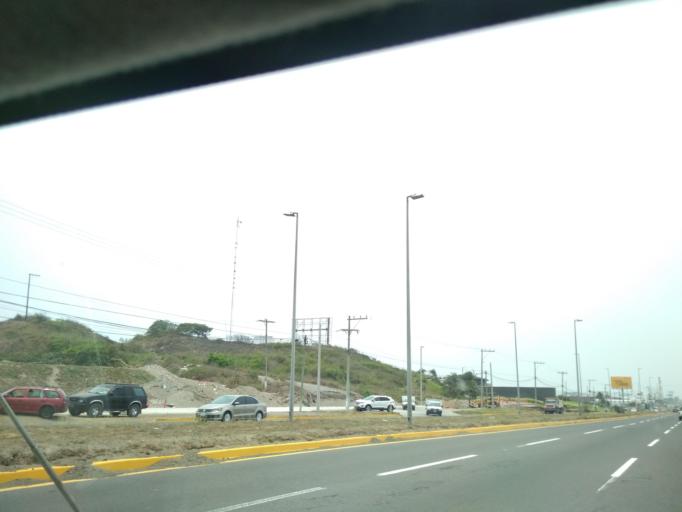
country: MX
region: Veracruz
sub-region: Alvarado
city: Playa de la Libertad
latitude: 19.0665
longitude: -96.0793
